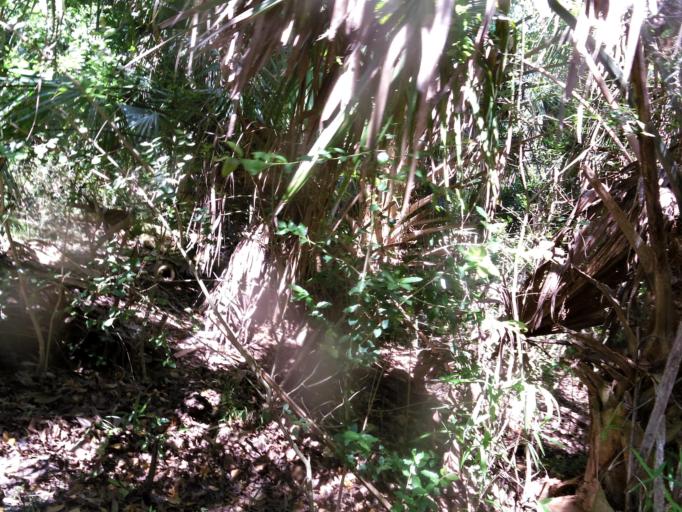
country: US
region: Florida
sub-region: Flagler County
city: Flagler Beach
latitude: 29.4200
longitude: -81.1396
